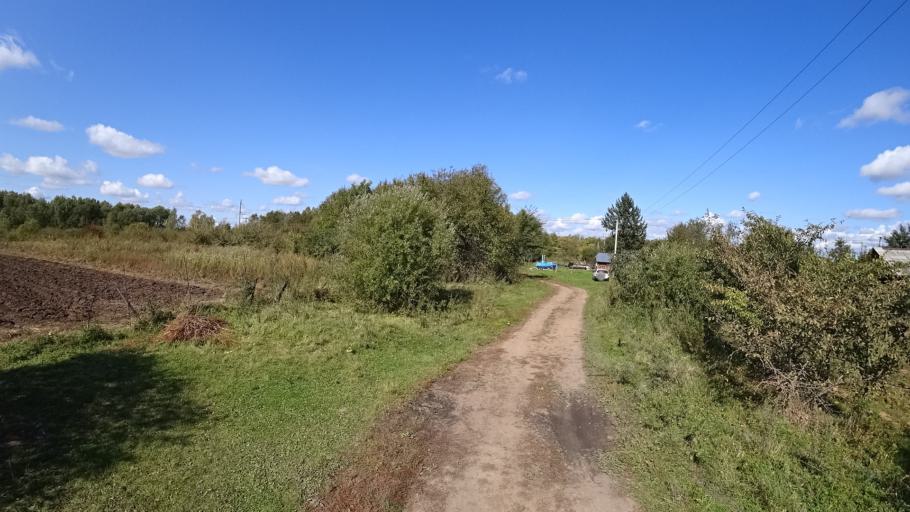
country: RU
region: Amur
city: Arkhara
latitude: 49.3994
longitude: 130.1263
